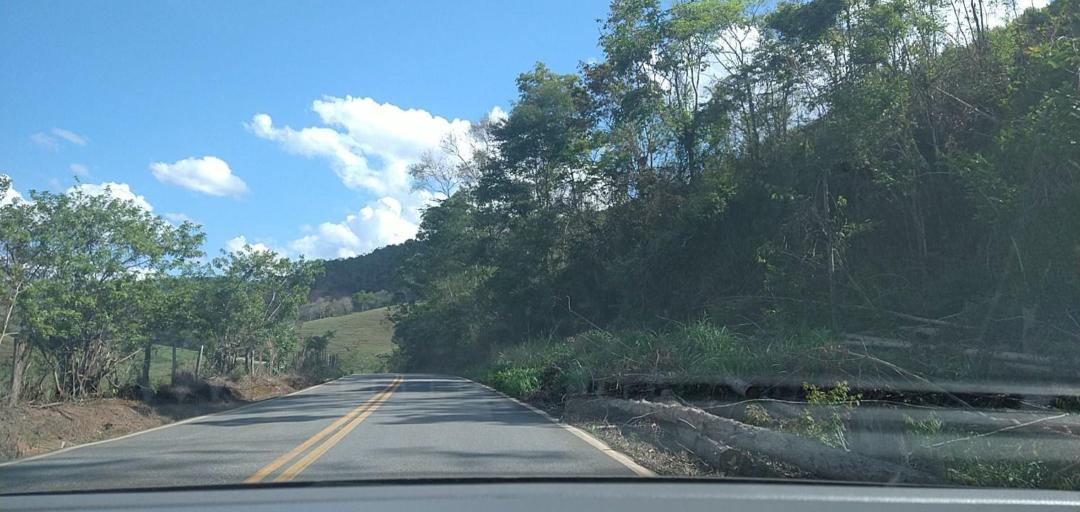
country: BR
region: Minas Gerais
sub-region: Rio Piracicaba
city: Rio Piracicaba
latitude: -19.9835
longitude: -43.1228
